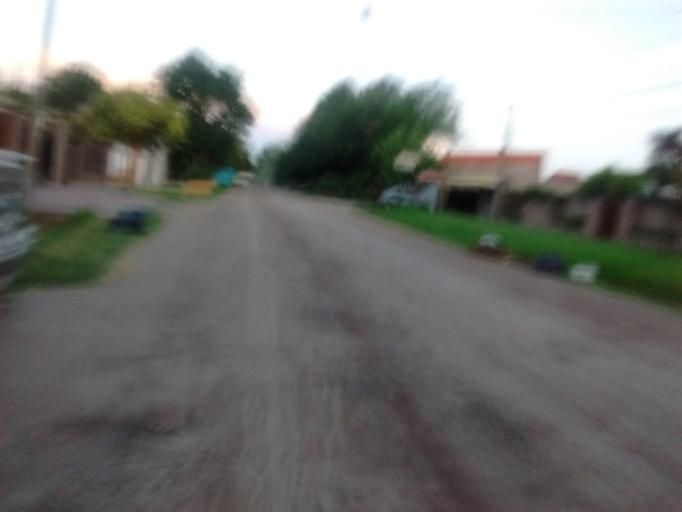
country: AR
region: Santa Fe
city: Funes
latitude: -32.9108
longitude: -60.8106
